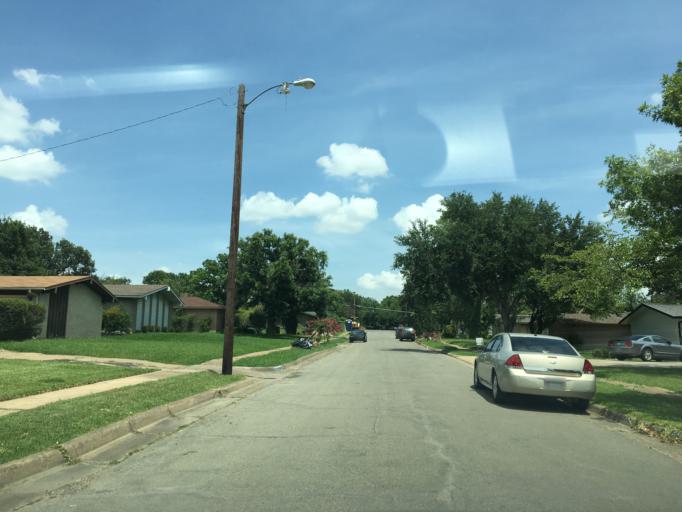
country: US
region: Texas
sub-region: Dallas County
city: Farmers Branch
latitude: 32.9131
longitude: -96.8587
